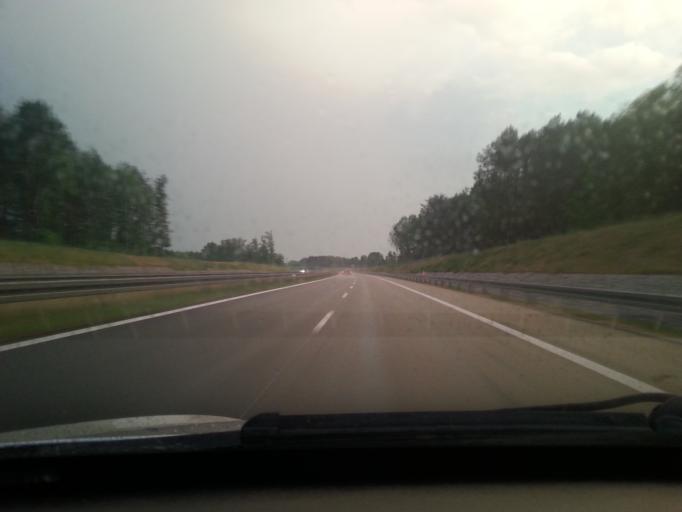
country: PL
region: Lodz Voivodeship
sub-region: Powiat pabianicki
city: Dobron
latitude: 51.6613
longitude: 19.2766
